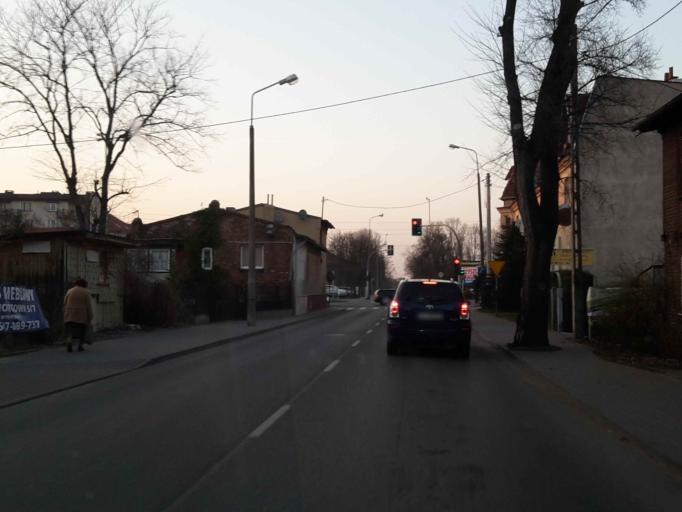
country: PL
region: Kujawsko-Pomorskie
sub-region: Torun
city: Torun
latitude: 53.0236
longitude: 18.6226
